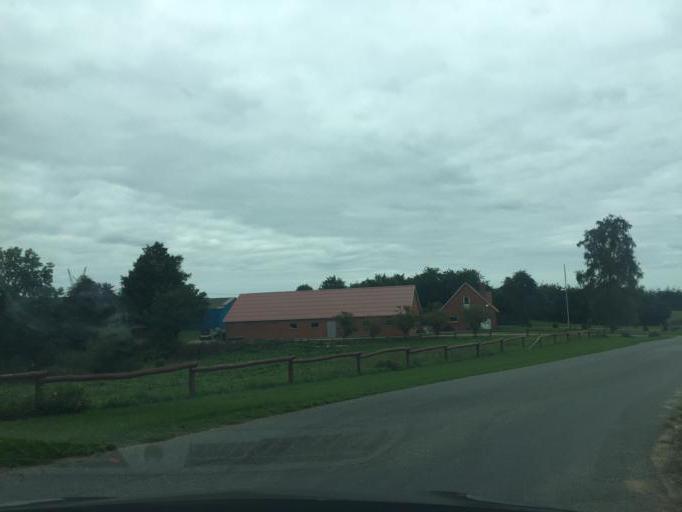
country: DK
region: South Denmark
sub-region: Assens Kommune
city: Tommerup Stationsby
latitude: 55.3774
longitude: 10.2187
